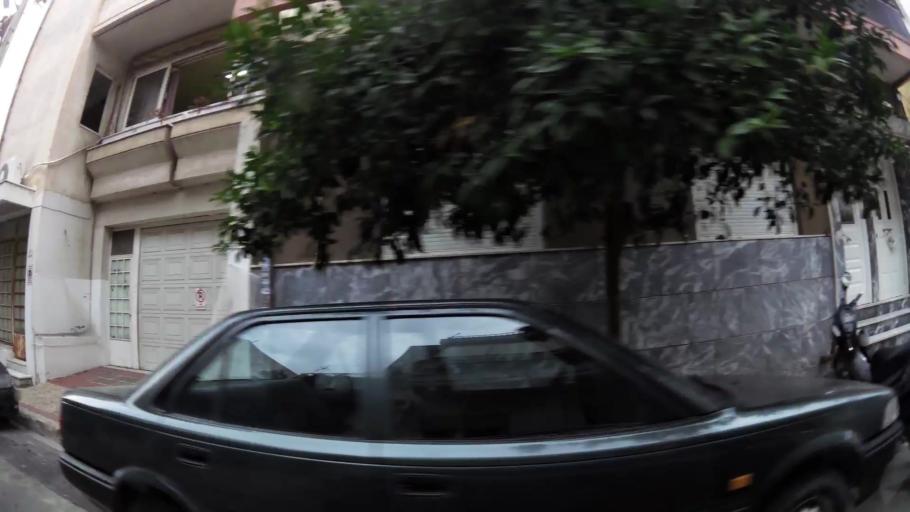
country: GR
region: Attica
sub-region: Nomos Piraios
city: Nikaia
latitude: 37.9636
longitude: 23.6510
